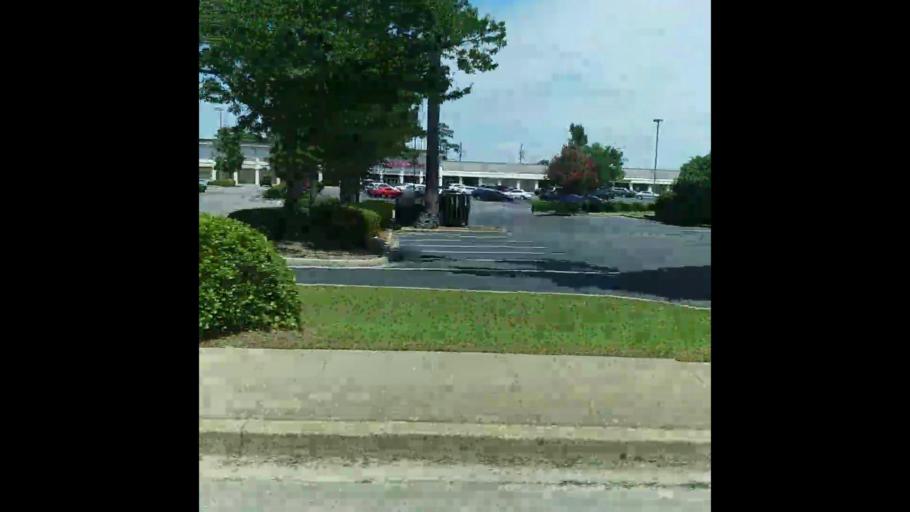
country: US
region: South Carolina
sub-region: Lexington County
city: West Columbia
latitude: 33.9871
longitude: -81.0565
